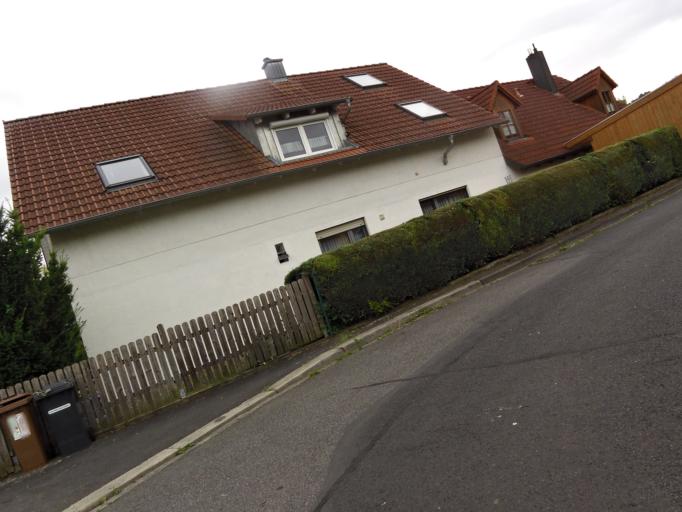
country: DE
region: Bavaria
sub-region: Regierungsbezirk Unterfranken
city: Reichenberg
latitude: 49.7606
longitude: 9.9327
